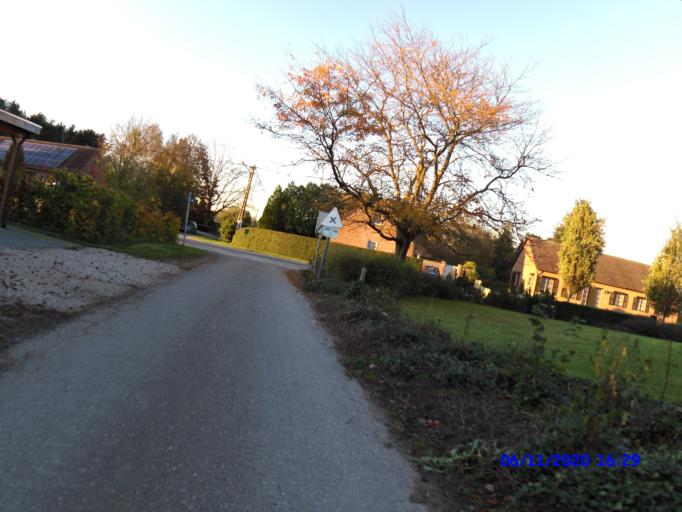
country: BE
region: Flanders
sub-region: Provincie Antwerpen
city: Mol
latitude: 51.1856
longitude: 5.0627
